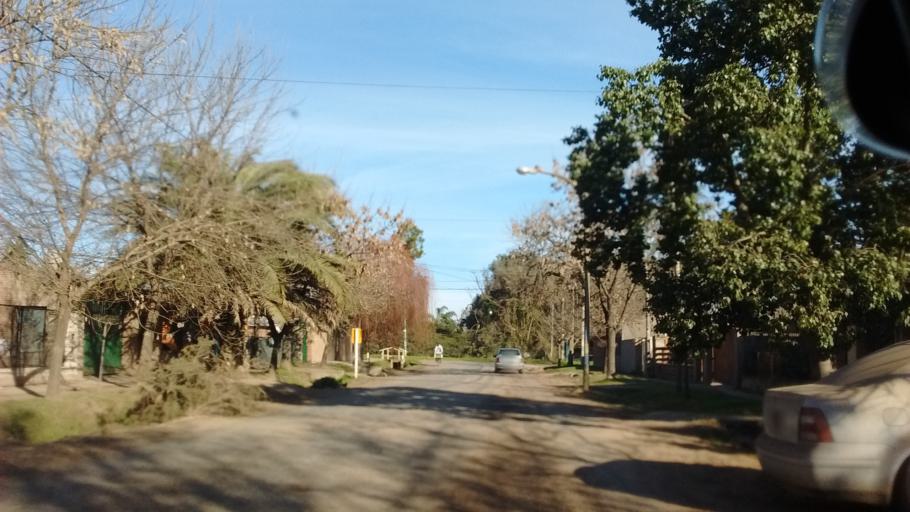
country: AR
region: Santa Fe
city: Funes
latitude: -32.9102
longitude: -60.8131
